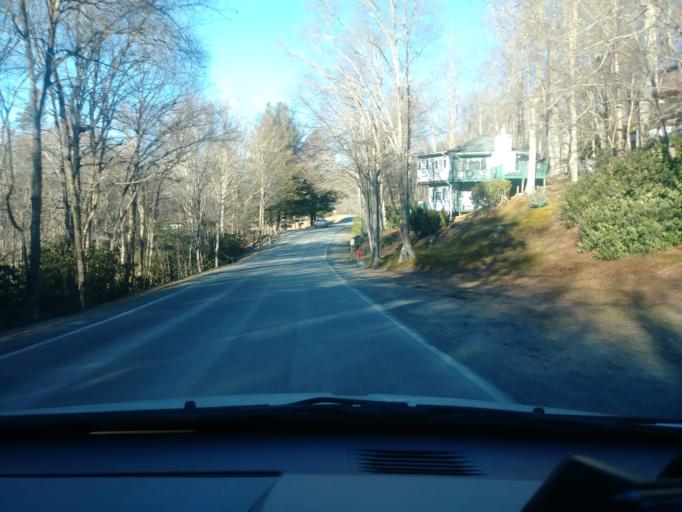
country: US
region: North Carolina
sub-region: Avery County
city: Banner Elk
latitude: 36.1294
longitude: -81.8513
